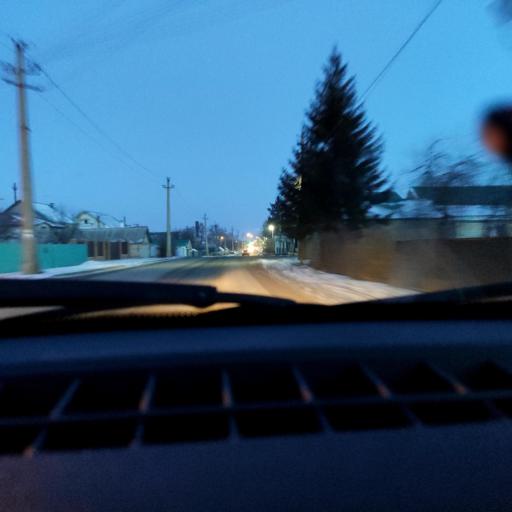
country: RU
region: Bashkortostan
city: Ufa
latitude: 54.6077
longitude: 55.9424
